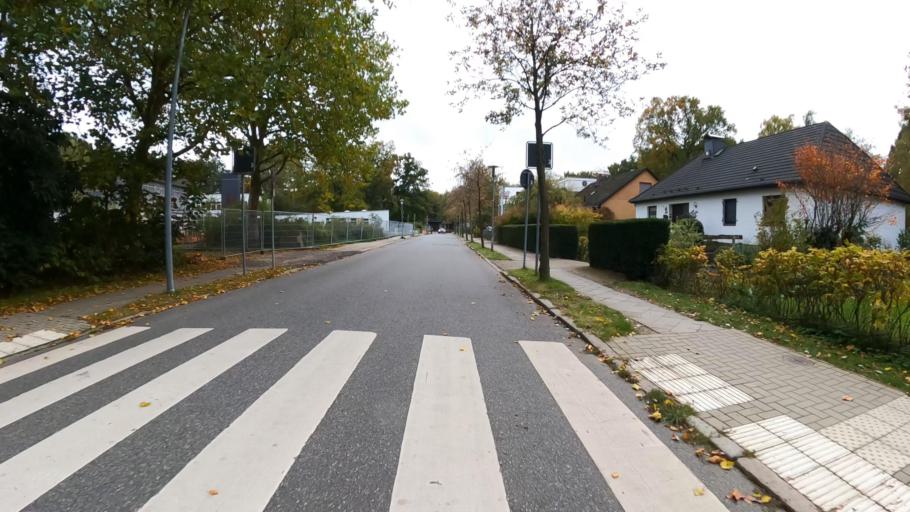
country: DE
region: Schleswig-Holstein
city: Ahrensburg
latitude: 53.6630
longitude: 10.2434
